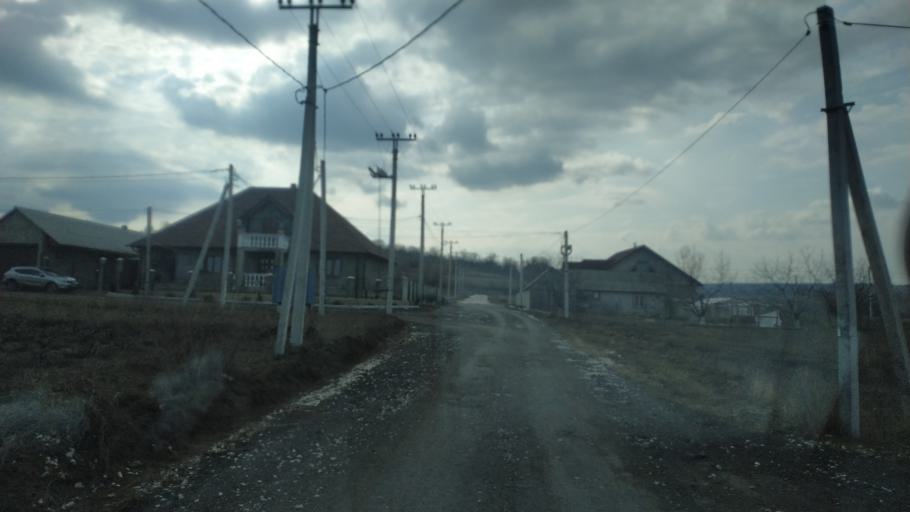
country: MD
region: Anenii Noi
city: Anenii Noi
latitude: 46.8977
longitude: 29.1330
